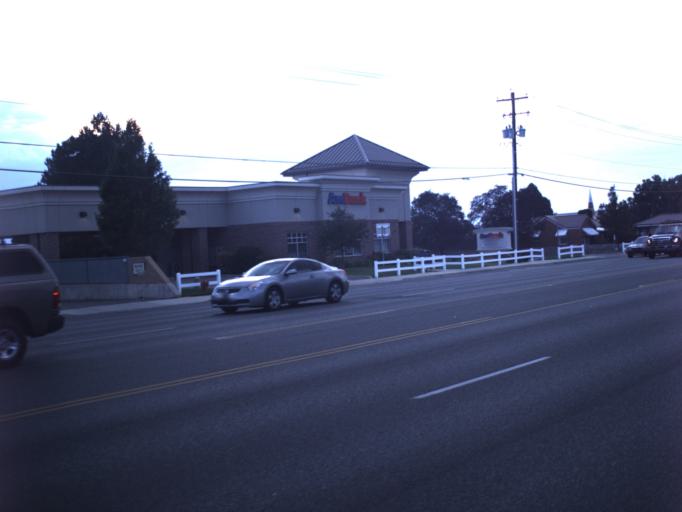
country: US
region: Utah
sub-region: Utah County
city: Lindon
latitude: 40.3346
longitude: -111.7140
